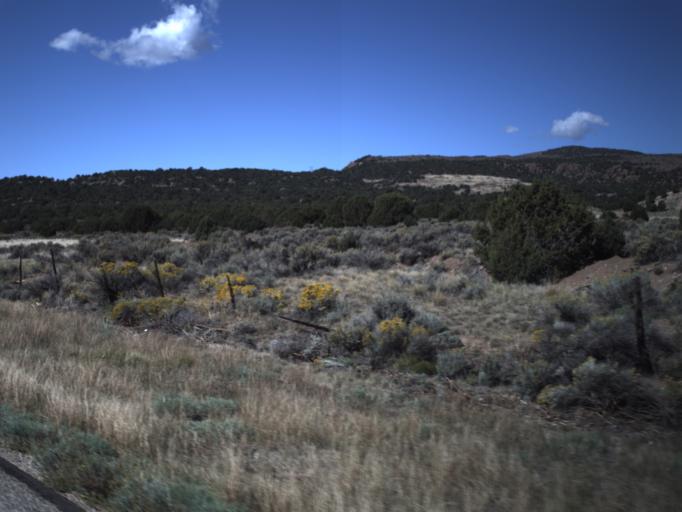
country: US
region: Utah
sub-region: Iron County
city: Cedar City
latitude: 37.6391
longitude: -113.2601
